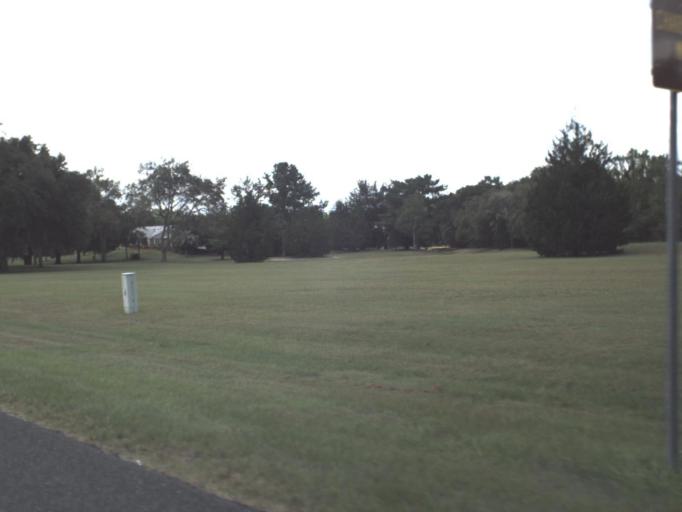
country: US
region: Florida
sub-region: Taylor County
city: Perry
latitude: 30.1635
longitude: -83.6250
